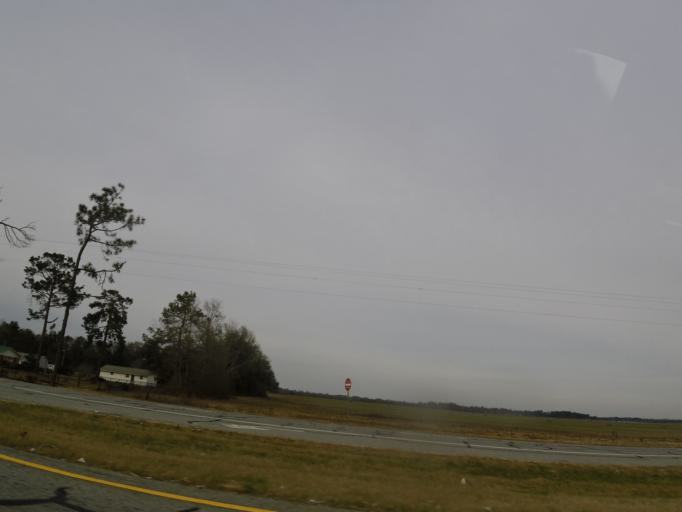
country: US
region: Georgia
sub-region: Decatur County
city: Bainbridge
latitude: 30.9365
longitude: -84.6591
